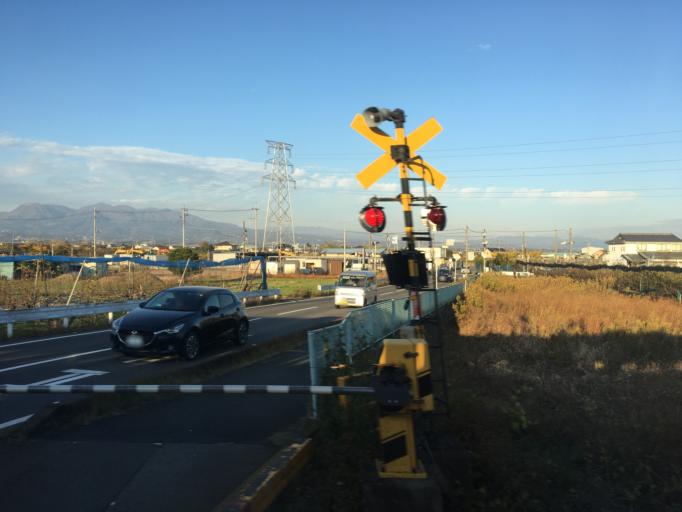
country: JP
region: Gunma
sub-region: Sawa-gun
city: Tamamura
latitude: 36.3626
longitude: 139.1239
